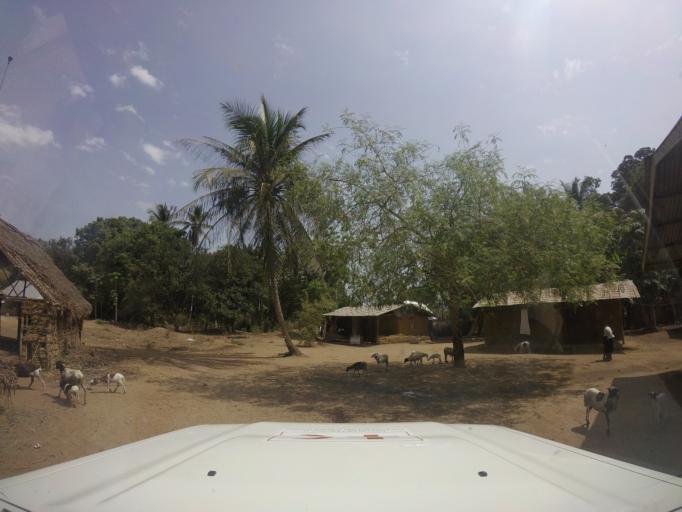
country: LR
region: Grand Cape Mount
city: Robertsport
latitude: 6.9437
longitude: -11.3515
